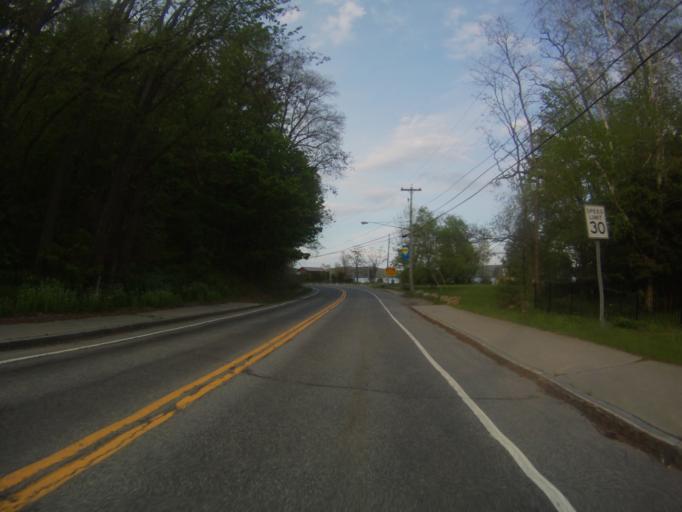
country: US
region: New York
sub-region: Essex County
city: Ticonderoga
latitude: 43.7455
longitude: -73.4979
